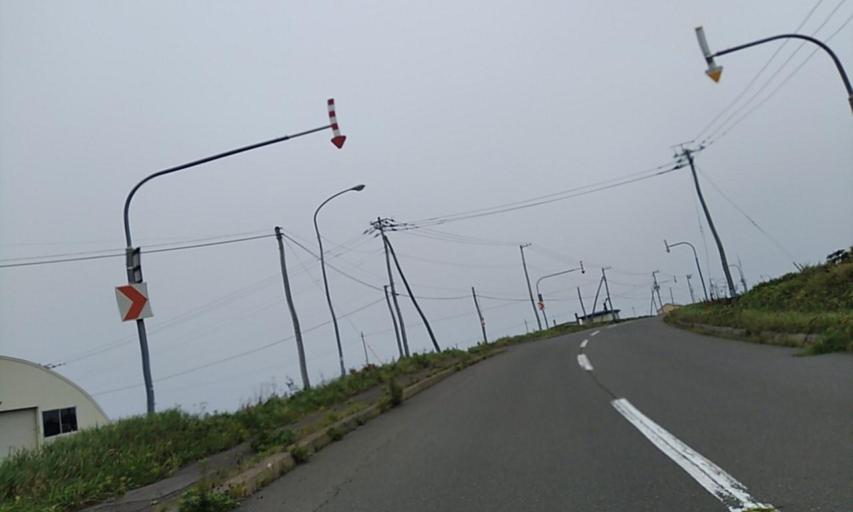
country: JP
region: Hokkaido
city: Nemuro
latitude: 43.3855
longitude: 145.7907
